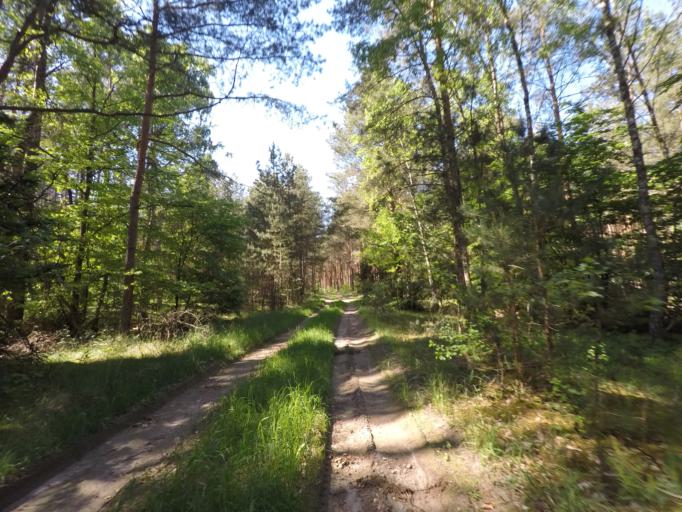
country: DE
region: Brandenburg
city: Melchow
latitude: 52.8205
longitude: 13.7545
